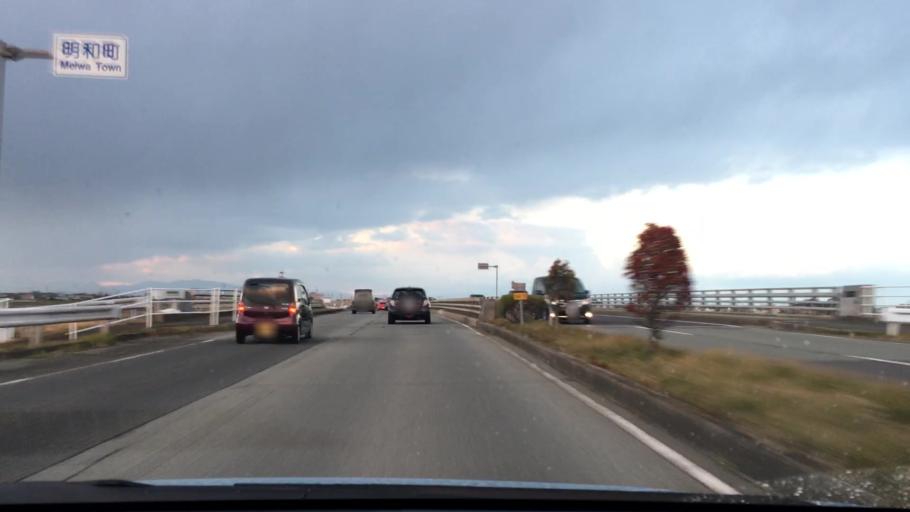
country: JP
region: Mie
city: Ise
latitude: 34.5506
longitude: 136.6571
